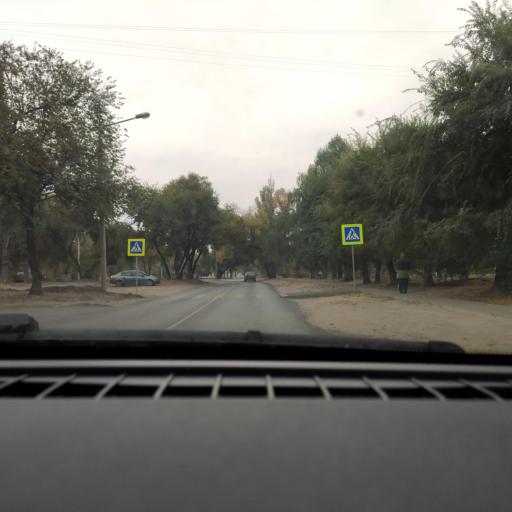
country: RU
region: Voronezj
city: Maslovka
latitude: 51.6157
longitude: 39.2412
